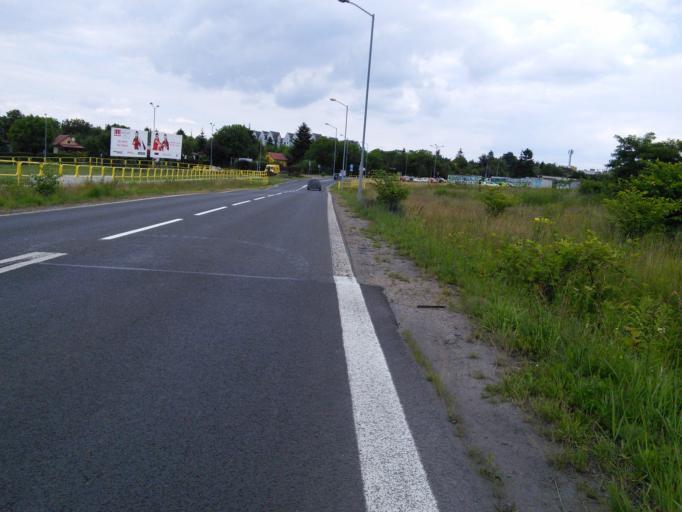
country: PL
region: Silesian Voivodeship
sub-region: Piekary Slaskie
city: Piekary Slaskie
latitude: 50.3733
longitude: 18.9355
